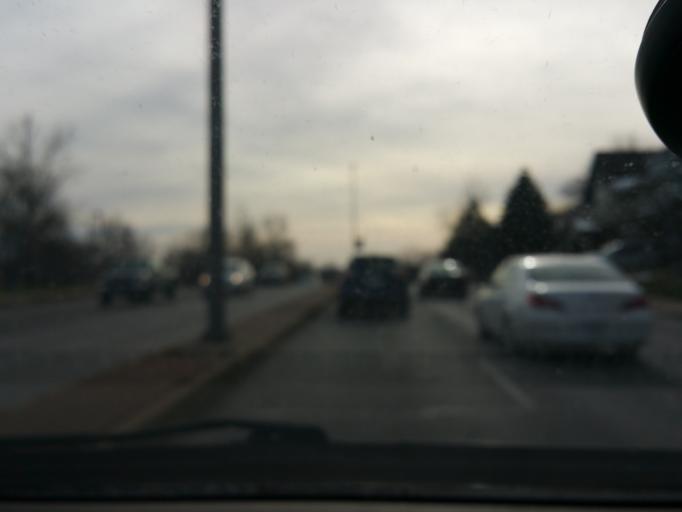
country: US
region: Missouri
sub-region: Jackson County
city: Kansas City
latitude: 39.0697
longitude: -94.5946
